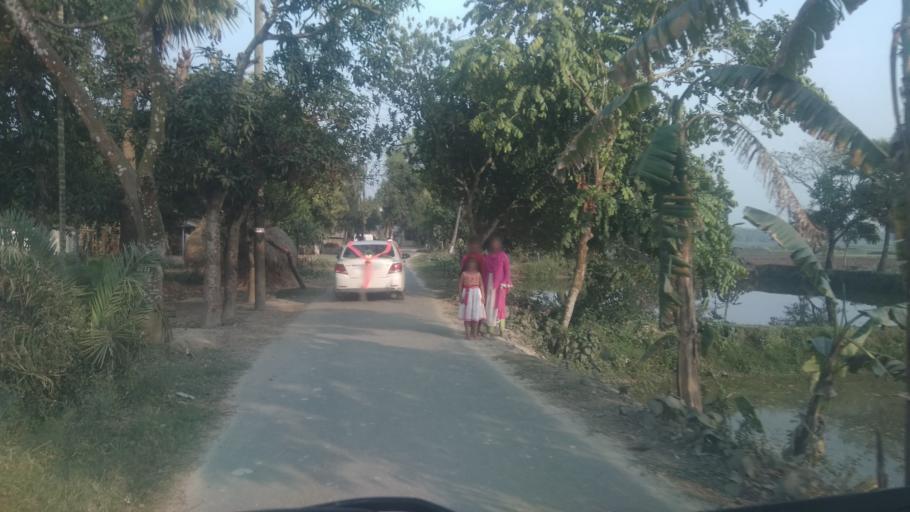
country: BD
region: Dhaka
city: Netrakona
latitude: 24.7752
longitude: 90.6069
